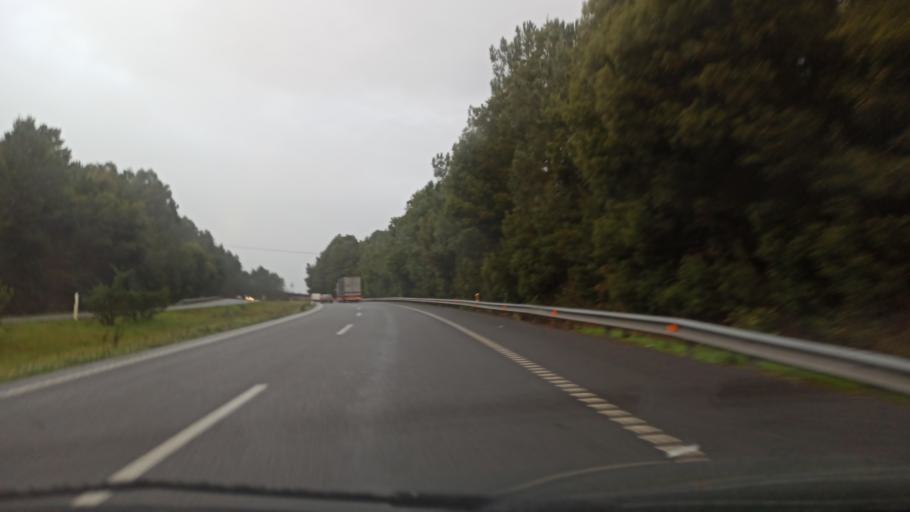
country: ES
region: Galicia
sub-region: Provincia da Coruna
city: Abegondo
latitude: 43.2667
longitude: -8.2972
